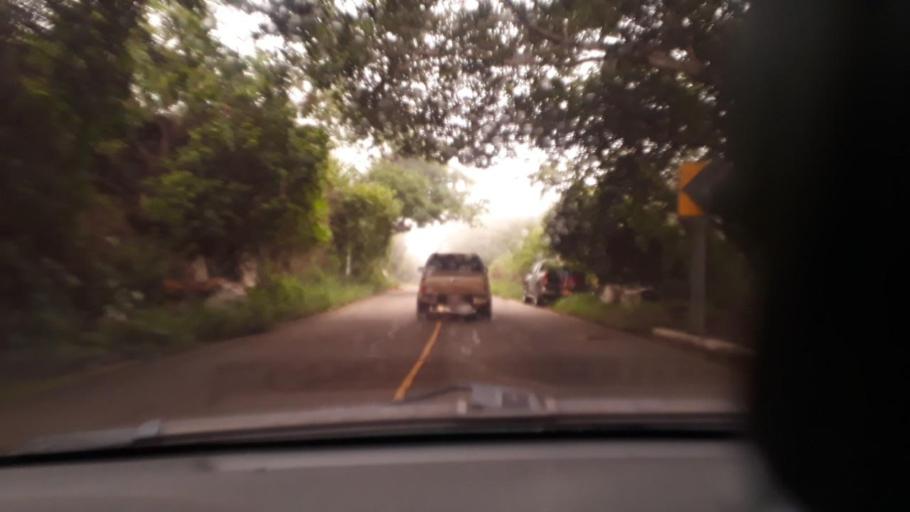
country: GT
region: Jutiapa
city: Jalpatagua
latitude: 14.1815
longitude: -90.0366
